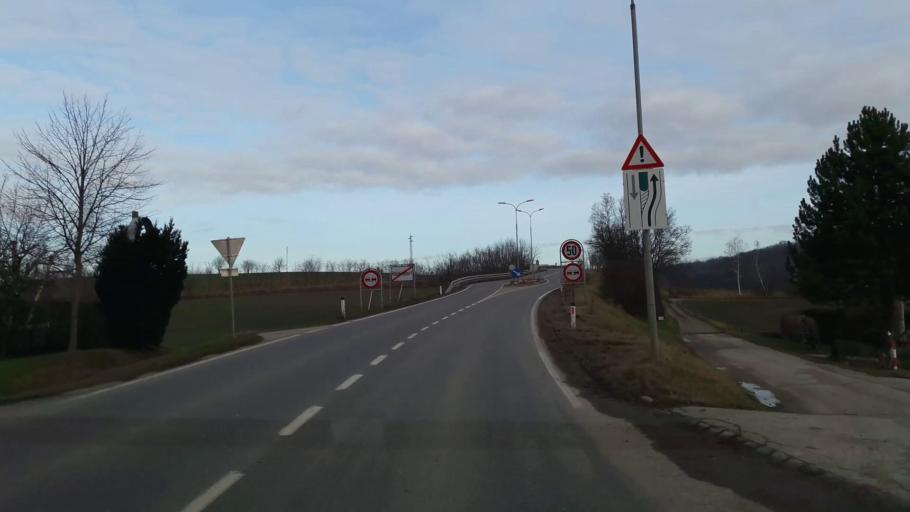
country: AT
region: Lower Austria
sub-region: Politischer Bezirk Mistelbach
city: Staatz
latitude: 48.6314
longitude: 16.5180
